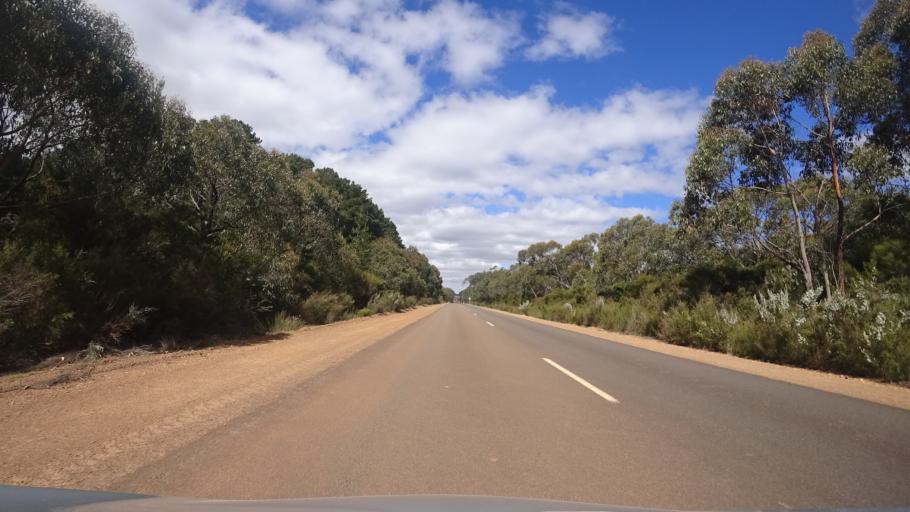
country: AU
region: South Australia
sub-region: Kangaroo Island
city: Kingscote
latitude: -35.7930
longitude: 136.9825
